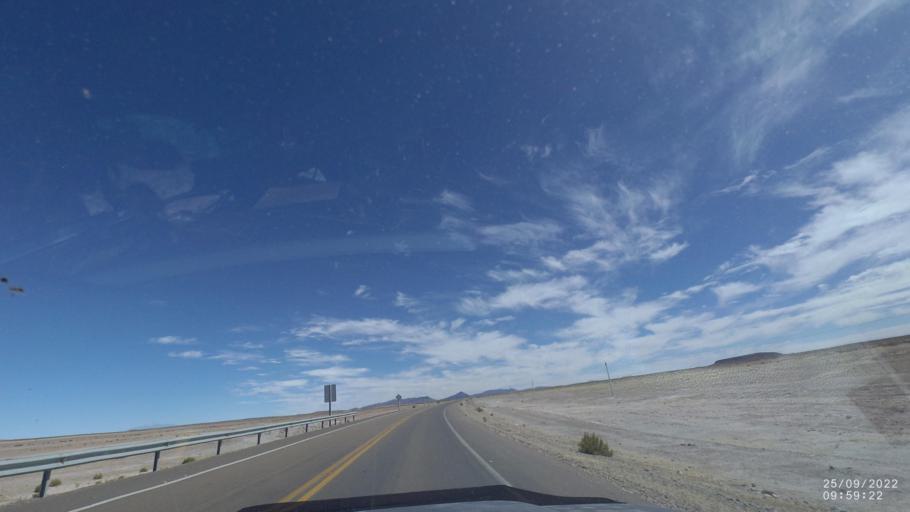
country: BO
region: Potosi
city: Colchani
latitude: -20.2933
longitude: -66.9374
